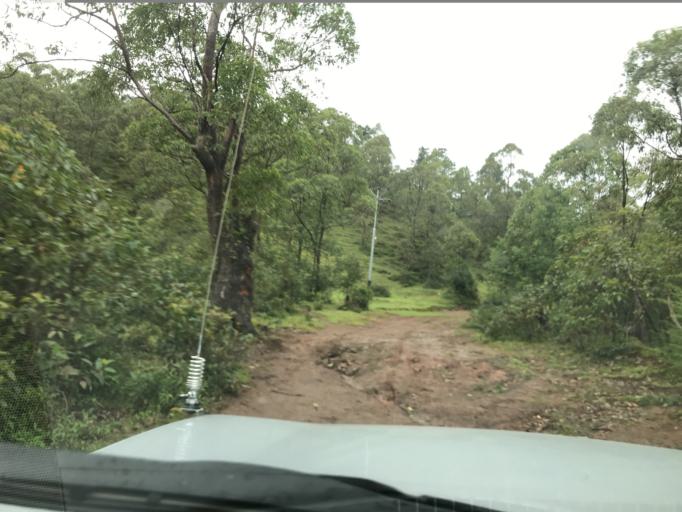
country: TL
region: Ainaro
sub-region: Ainaro
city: Ainaro
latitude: -8.8773
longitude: 125.5535
